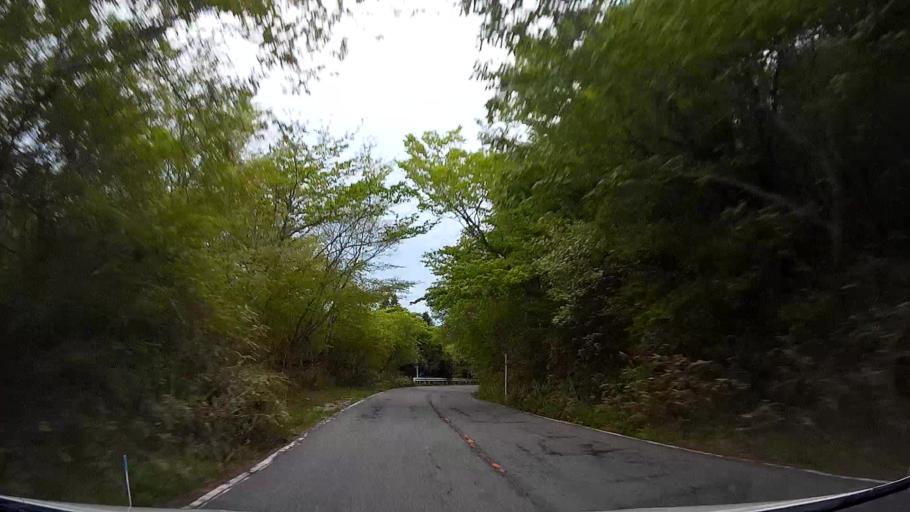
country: JP
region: Kanagawa
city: Hakone
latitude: 35.1842
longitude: 139.0613
